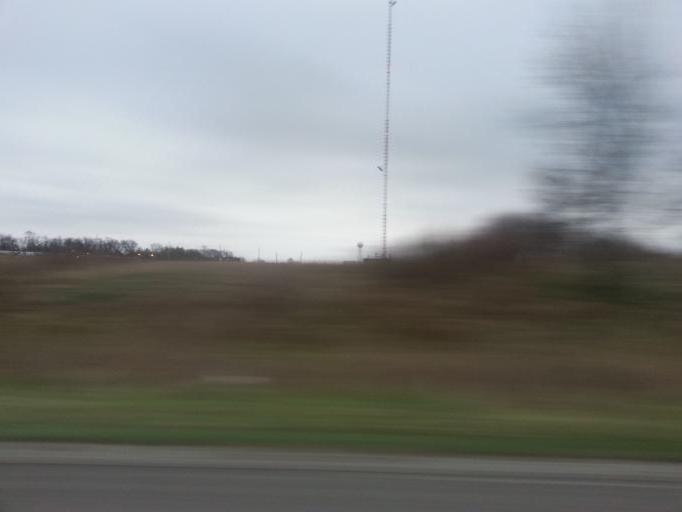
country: US
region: Iowa
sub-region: Linn County
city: Hiawatha
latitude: 42.0561
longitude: -91.6991
